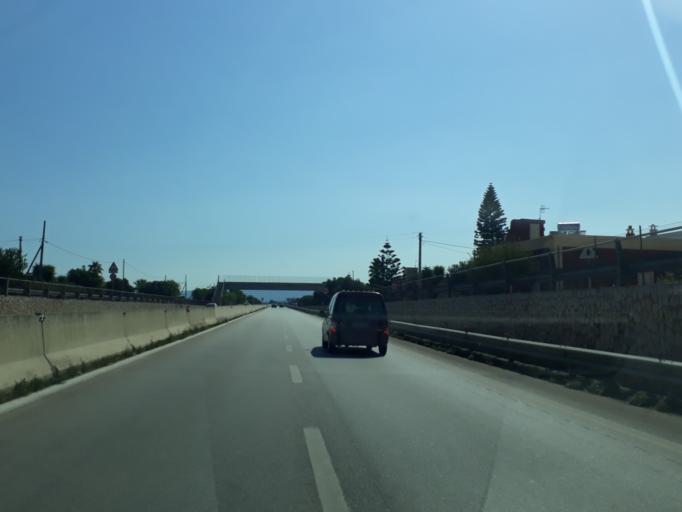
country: IT
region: Apulia
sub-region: Provincia di Brindisi
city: Fasano
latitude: 40.8698
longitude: 17.3437
